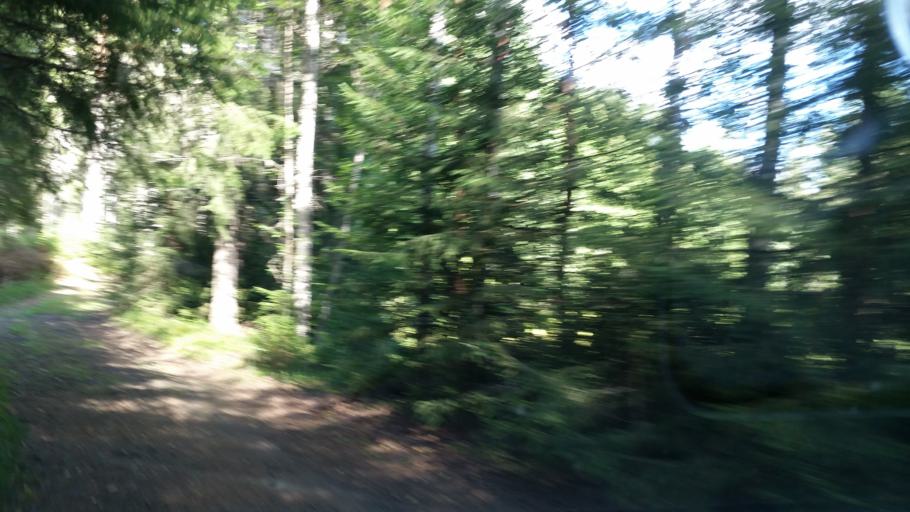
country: SE
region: Gaevleborg
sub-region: Ljusdals Kommun
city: Ljusdal
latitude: 61.9722
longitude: 16.3261
